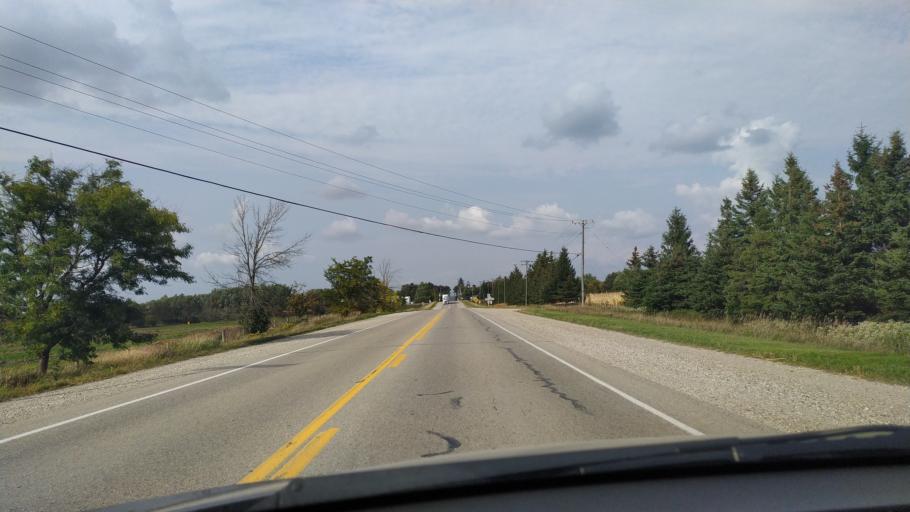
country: CA
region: Ontario
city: Stratford
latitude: 43.3624
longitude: -80.8369
